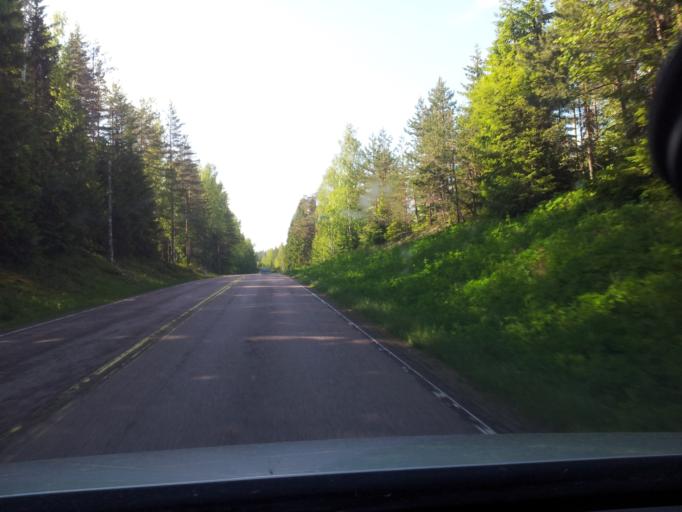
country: FI
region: South Karelia
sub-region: Lappeenranta
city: Luumaeki
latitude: 60.9706
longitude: 27.5593
